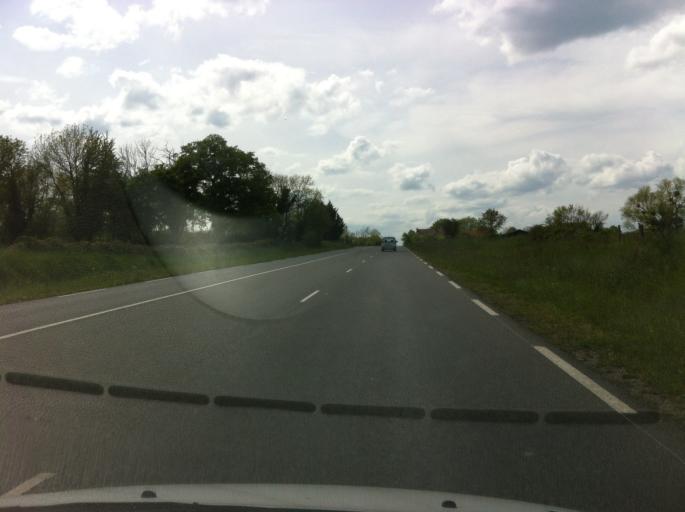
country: FR
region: Auvergne
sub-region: Departement de l'Allier
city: Saint-Pourcain-sur-Sioule
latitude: 46.3133
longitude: 3.2187
